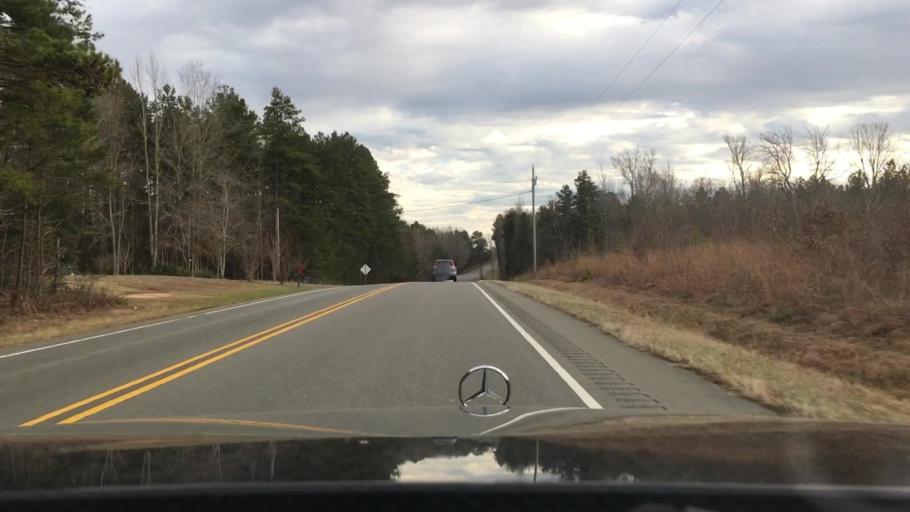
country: US
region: North Carolina
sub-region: Alamance County
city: Mebane
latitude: 36.2366
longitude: -79.1892
